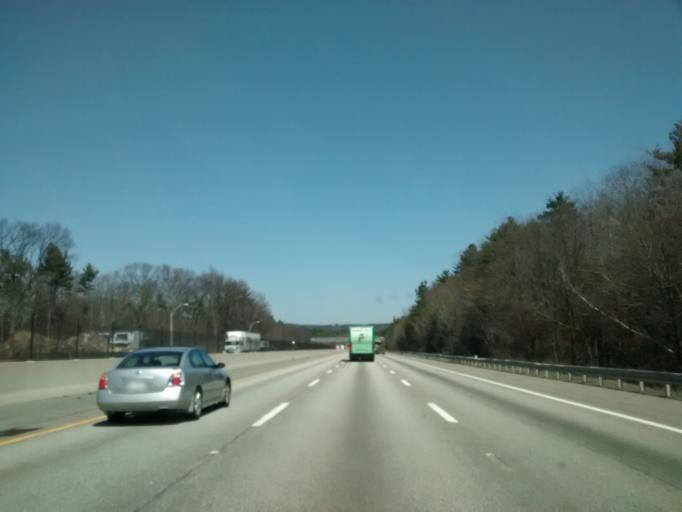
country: US
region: Massachusetts
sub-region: Worcester County
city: Westborough
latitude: 42.2465
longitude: -71.5894
